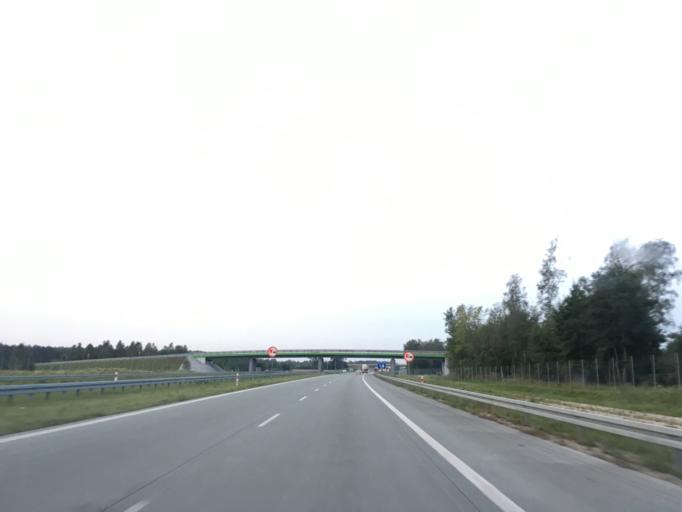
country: PL
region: Lodz Voivodeship
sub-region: Powiat lodzki wschodni
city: Andrespol
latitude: 51.7138
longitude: 19.6079
